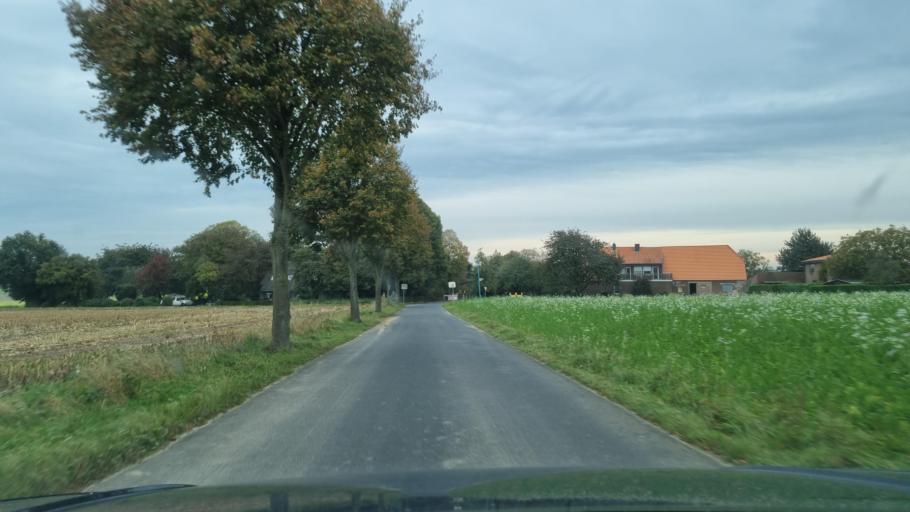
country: DE
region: North Rhine-Westphalia
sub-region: Regierungsbezirk Dusseldorf
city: Goch
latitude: 51.7440
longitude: 6.2060
